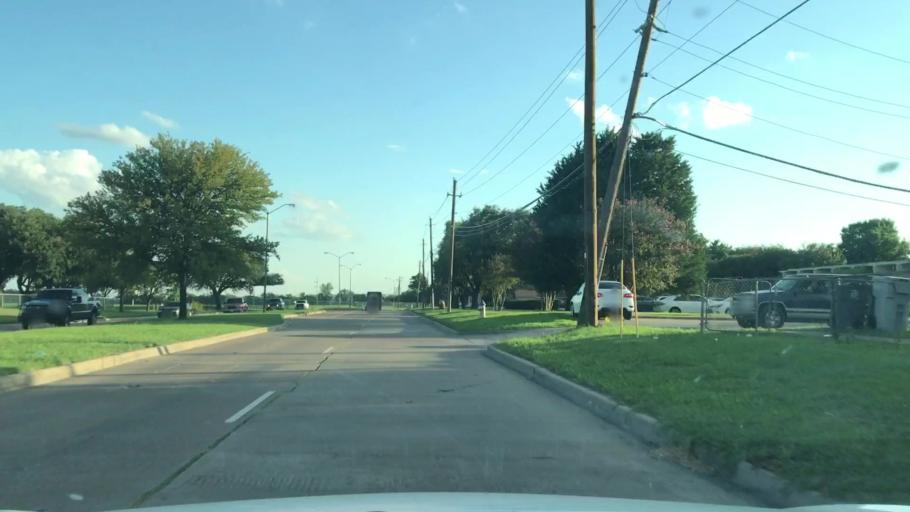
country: US
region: Texas
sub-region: Dallas County
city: Mesquite
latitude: 32.8130
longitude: -96.6655
